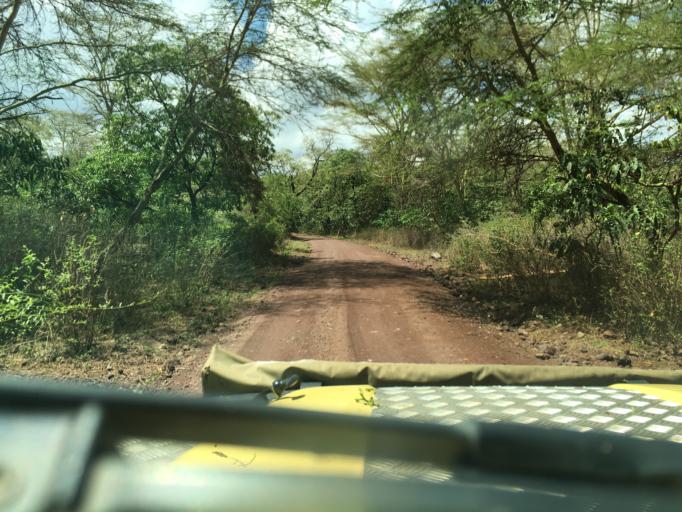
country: TZ
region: Arusha
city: Mto wa Mbu
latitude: -3.4083
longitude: 35.8226
